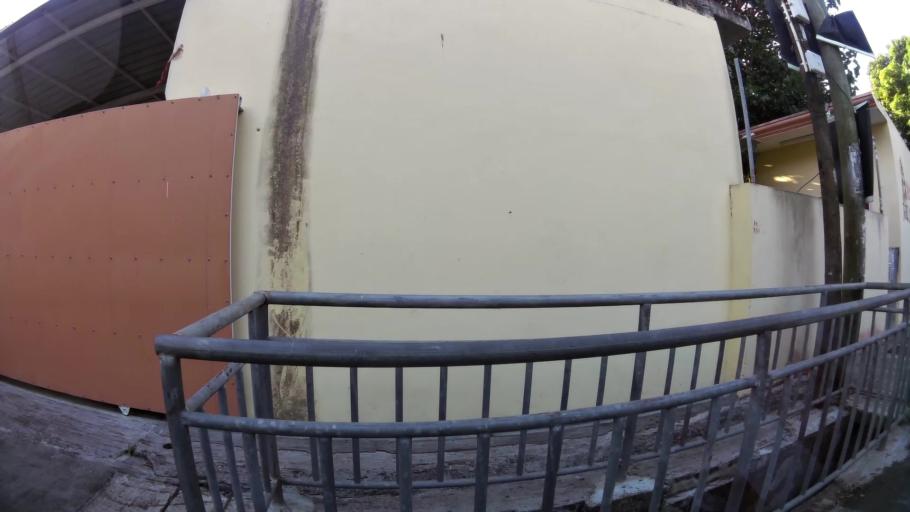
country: MU
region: Port Louis
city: Port Louis
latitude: -20.1780
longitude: 57.5127
